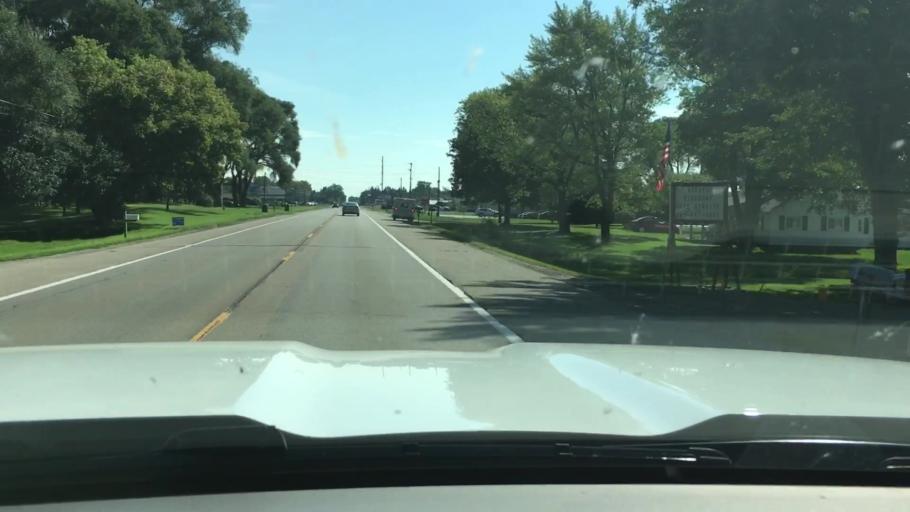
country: US
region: Michigan
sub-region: Gratiot County
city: Saint Louis
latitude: 43.4079
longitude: -84.6402
